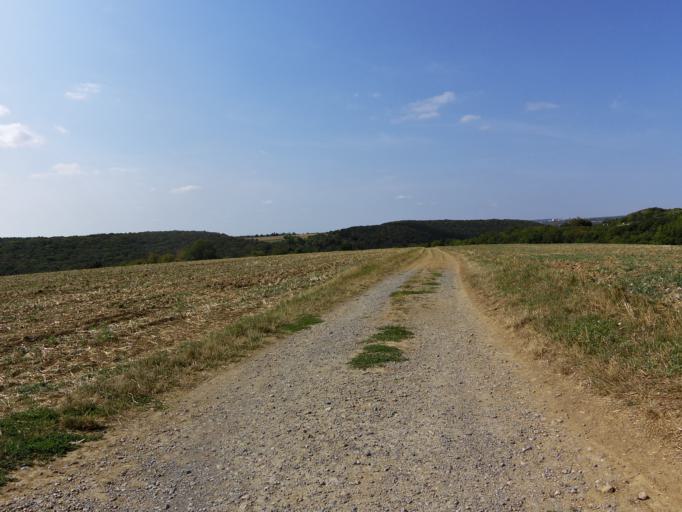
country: DE
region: Bavaria
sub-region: Regierungsbezirk Unterfranken
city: Theilheim
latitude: 49.7579
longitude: 10.0217
